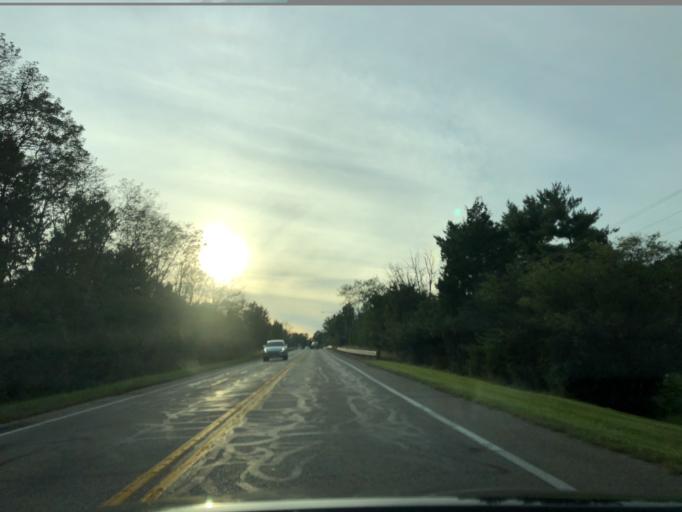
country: US
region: Ohio
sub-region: Hamilton County
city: The Village of Indian Hill
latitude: 39.2490
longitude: -84.3029
